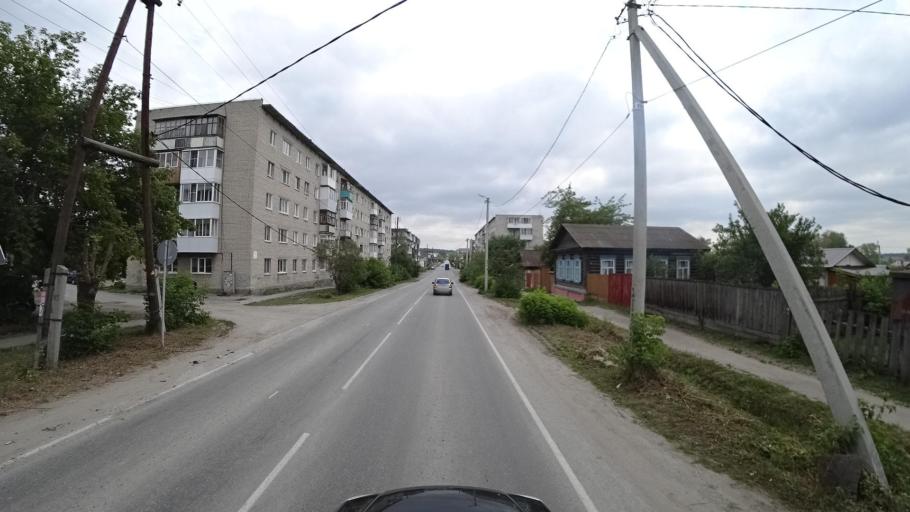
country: RU
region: Sverdlovsk
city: Kamyshlov
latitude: 56.8399
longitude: 62.7128
